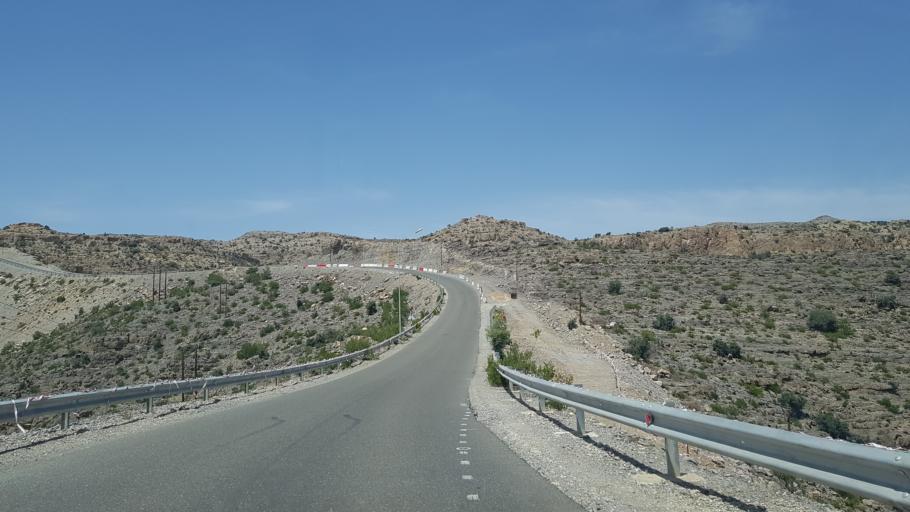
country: OM
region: Muhafazat ad Dakhiliyah
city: Izki
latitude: 23.0971
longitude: 57.6743
